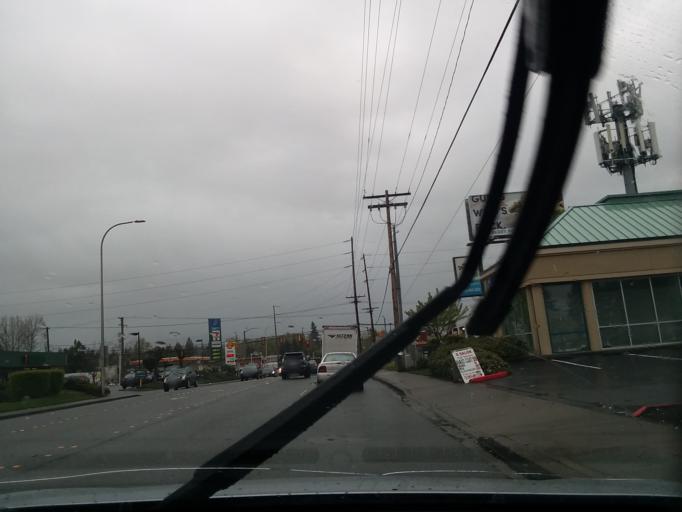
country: US
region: Washington
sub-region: King County
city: Fairwood
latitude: 47.4886
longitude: -122.1657
